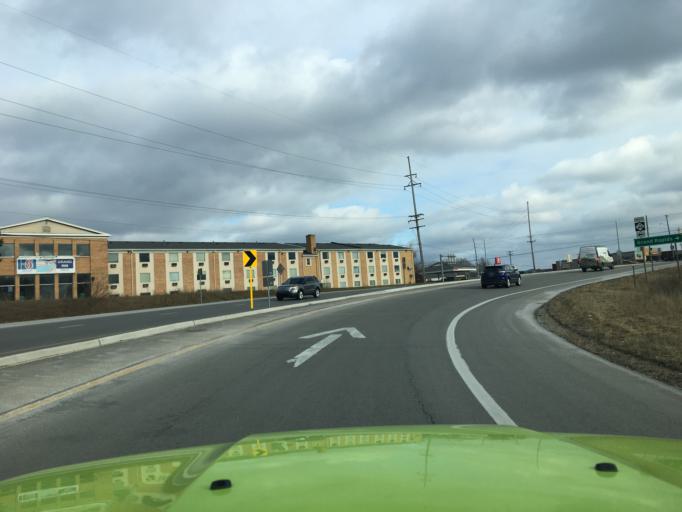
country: US
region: Michigan
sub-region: Kent County
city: Comstock Park
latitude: 43.0210
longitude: -85.6363
